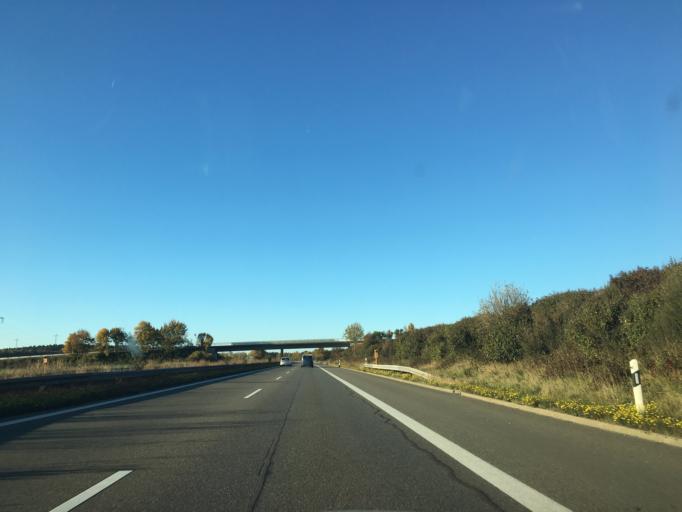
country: DE
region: Baden-Wuerttemberg
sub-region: Freiburg Region
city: Deisslingen
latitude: 48.1111
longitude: 8.5824
